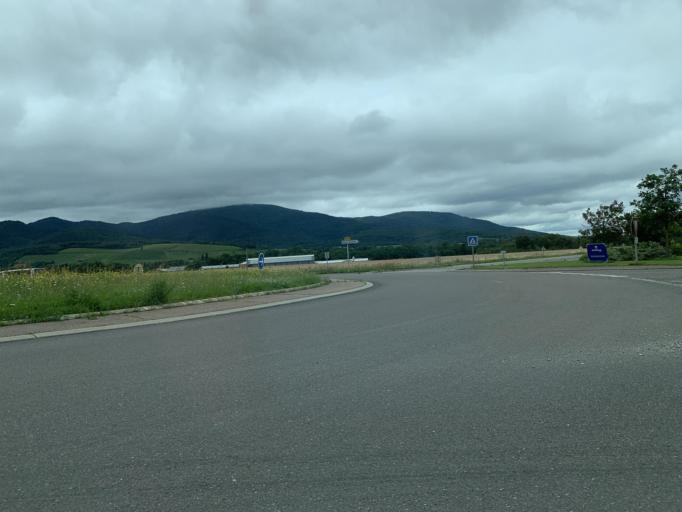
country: FR
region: Alsace
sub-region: Departement du Haut-Rhin
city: Cernay
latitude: 47.7952
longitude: 7.1585
